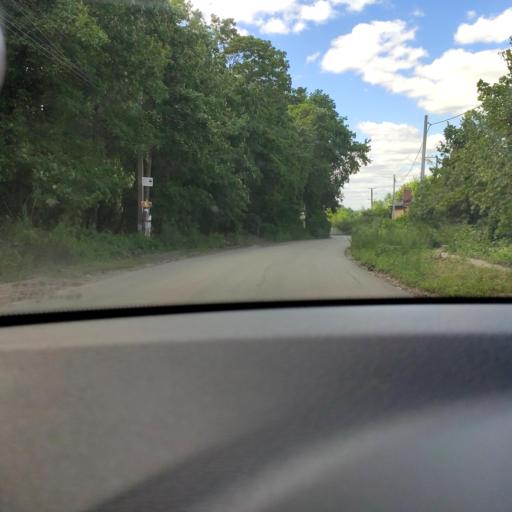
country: RU
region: Samara
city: Samara
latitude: 53.2969
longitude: 50.2121
